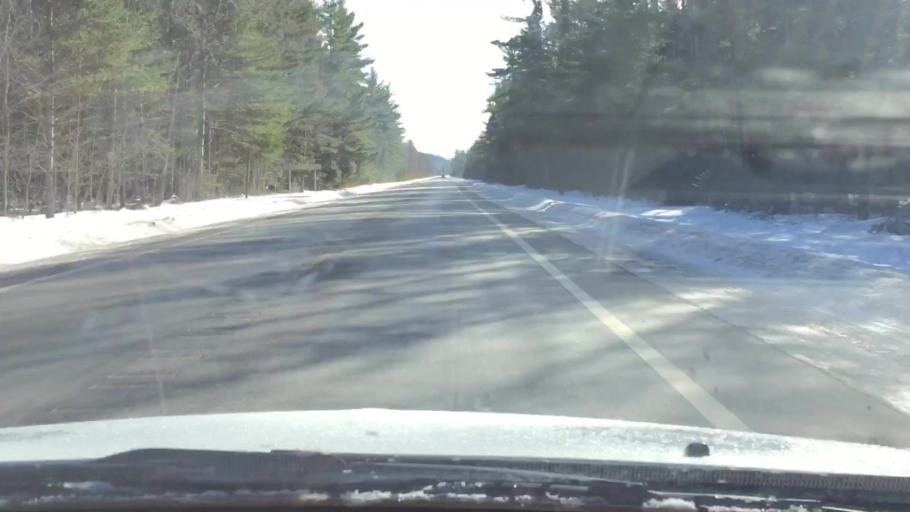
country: US
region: Michigan
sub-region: Antrim County
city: Mancelona
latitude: 45.0322
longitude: -85.0670
